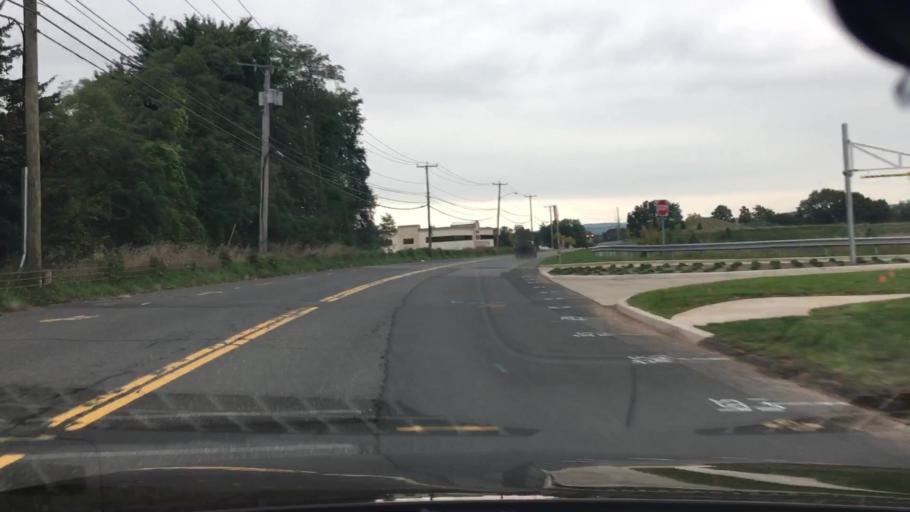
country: US
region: Connecticut
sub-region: Hartford County
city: Kensington
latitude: 41.5985
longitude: -72.7214
